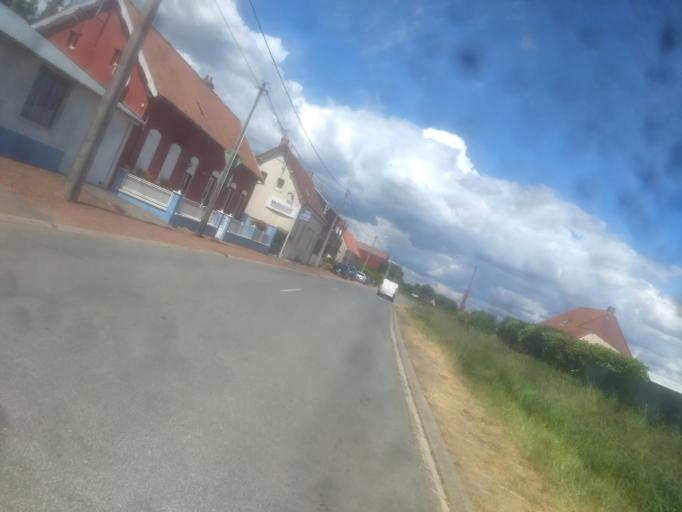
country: FR
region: Nord-Pas-de-Calais
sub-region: Departement du Pas-de-Calais
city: Croisilles
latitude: 50.2265
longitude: 2.8365
